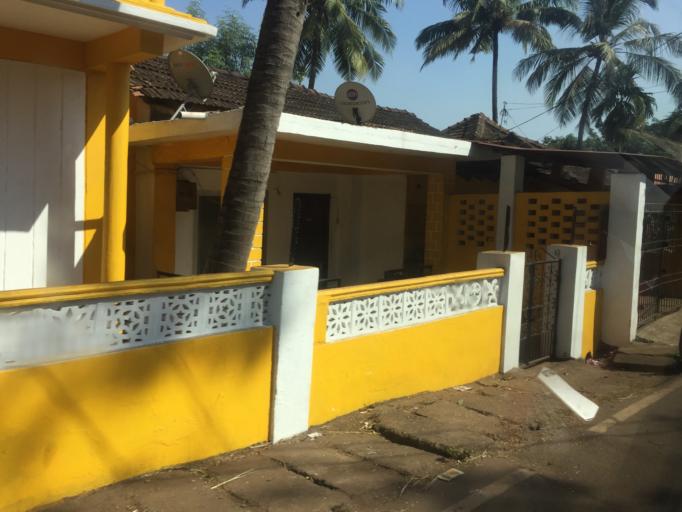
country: IN
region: Goa
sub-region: South Goa
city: Vasco Da Gama
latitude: 15.3879
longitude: 73.8178
